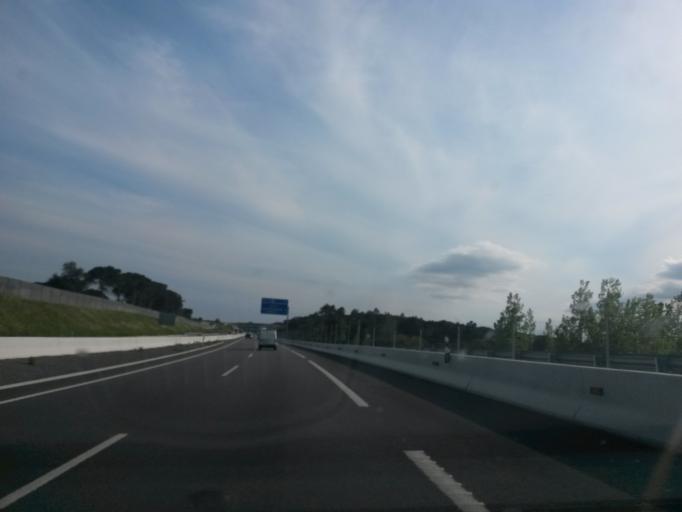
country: ES
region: Catalonia
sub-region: Provincia de Girona
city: Sils
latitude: 41.8440
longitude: 2.7609
